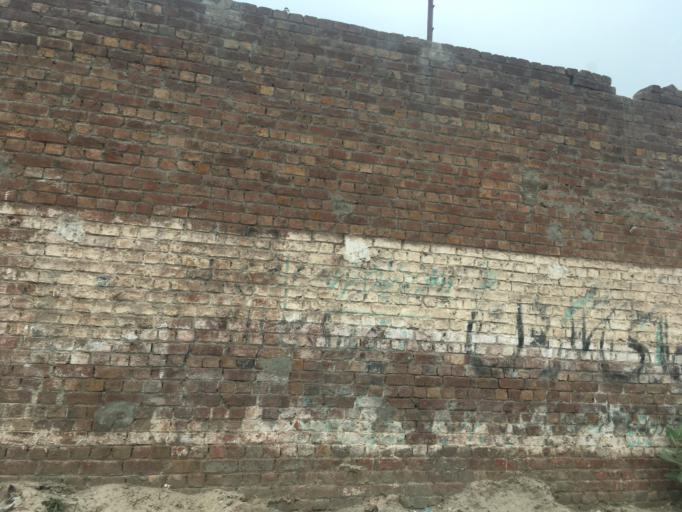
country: PK
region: Punjab
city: Lahore
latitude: 31.6120
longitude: 74.3506
